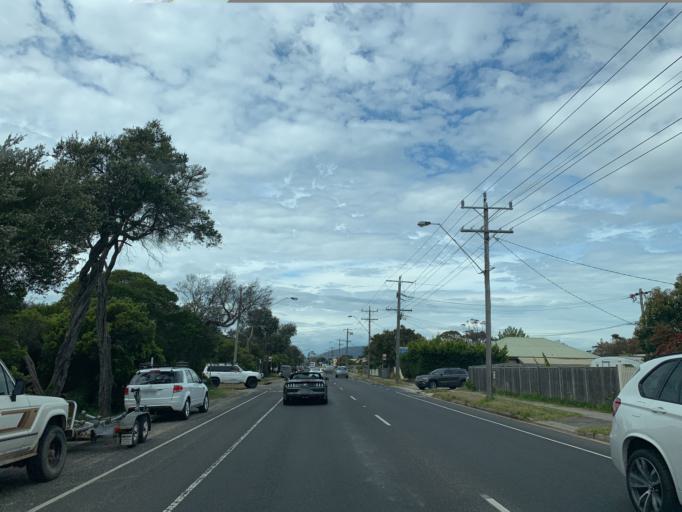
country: AU
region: Victoria
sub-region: Mornington Peninsula
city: Tootgarook
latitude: -38.3679
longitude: 144.8586
